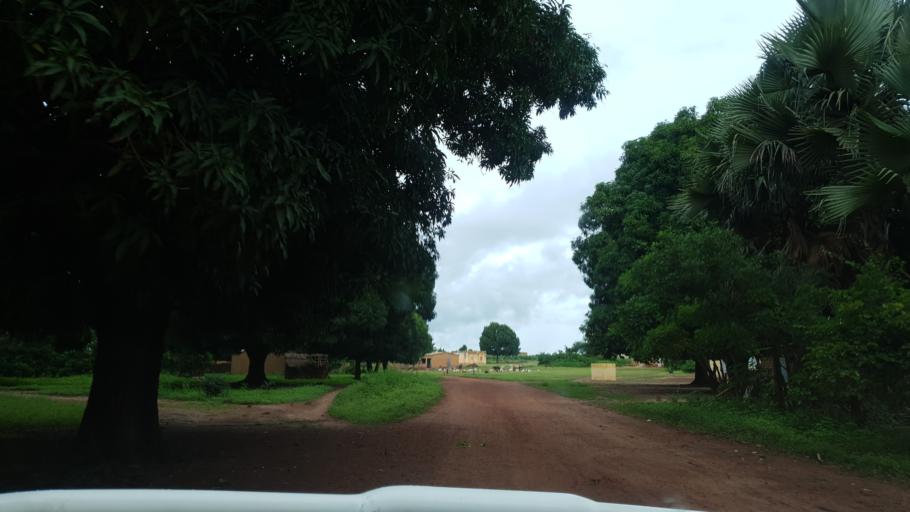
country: ML
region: Sikasso
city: Sikasso
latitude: 11.6745
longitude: -6.1706
